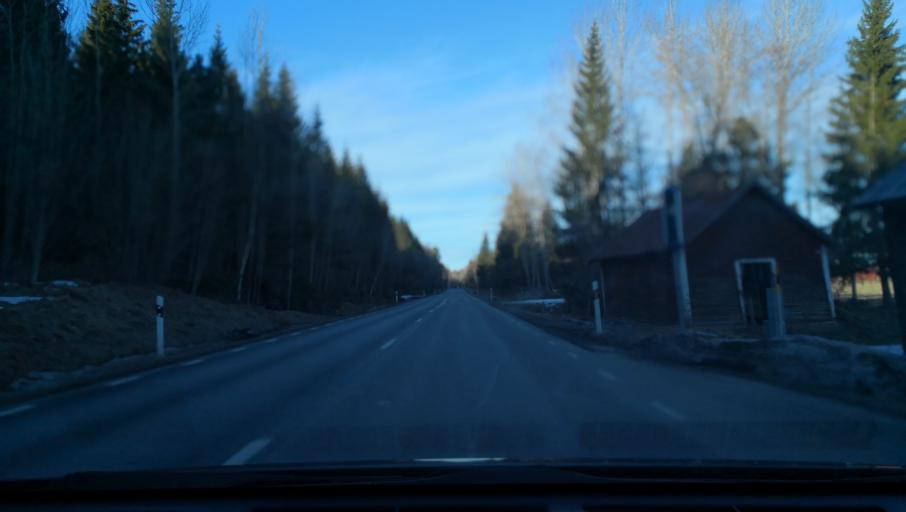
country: SE
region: Uppsala
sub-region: Osthammars Kommun
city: Gimo
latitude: 60.1950
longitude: 18.1913
